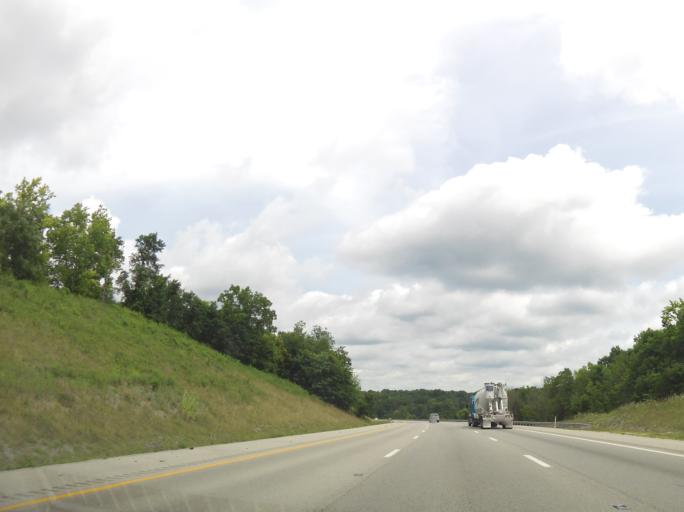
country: US
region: Kentucky
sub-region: Grant County
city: Williamstown
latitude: 38.4354
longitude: -84.5706
